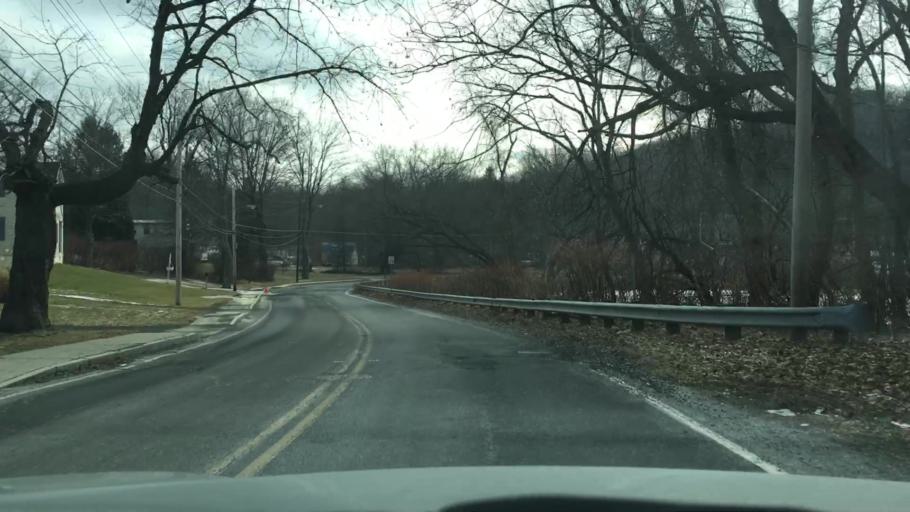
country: US
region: Massachusetts
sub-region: Berkshire County
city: Lee
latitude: 42.3135
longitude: -73.2460
